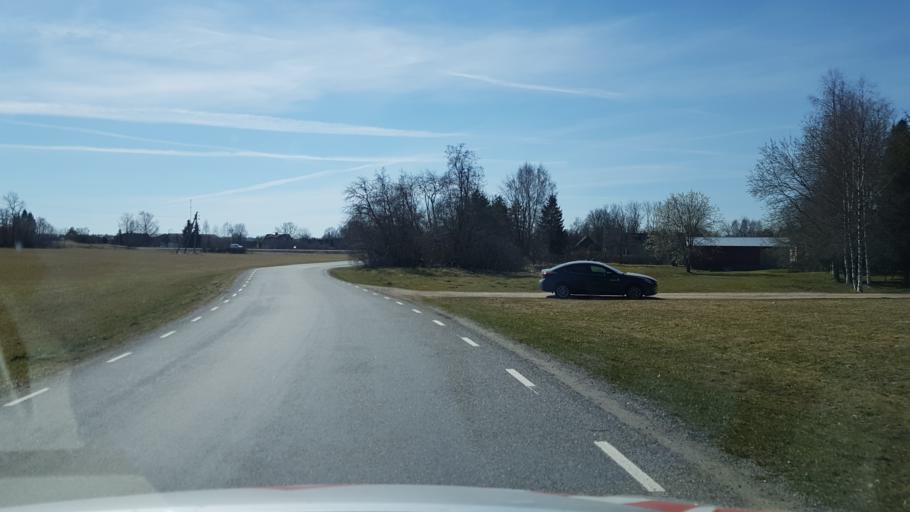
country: EE
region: Laeaene-Virumaa
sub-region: Vinni vald
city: Vinni
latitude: 59.2831
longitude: 26.4244
